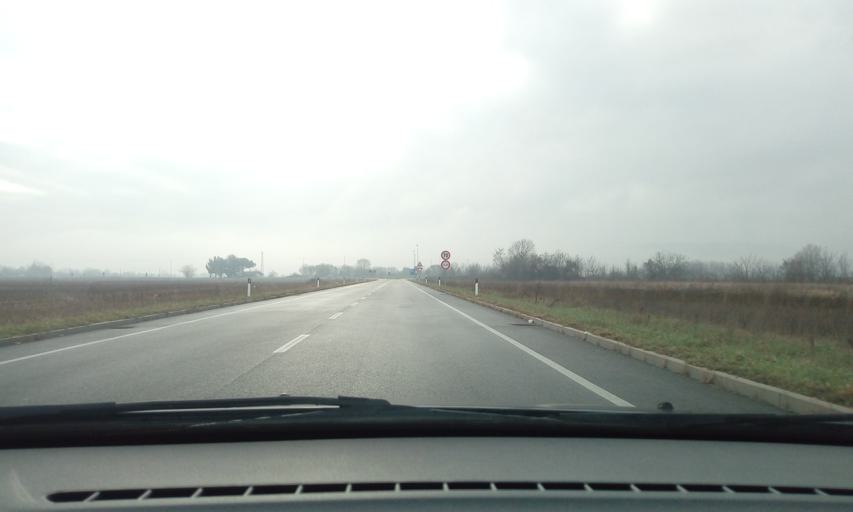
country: IT
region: Friuli Venezia Giulia
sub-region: Provincia di Gorizia
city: Mossa
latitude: 45.9272
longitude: 13.5545
